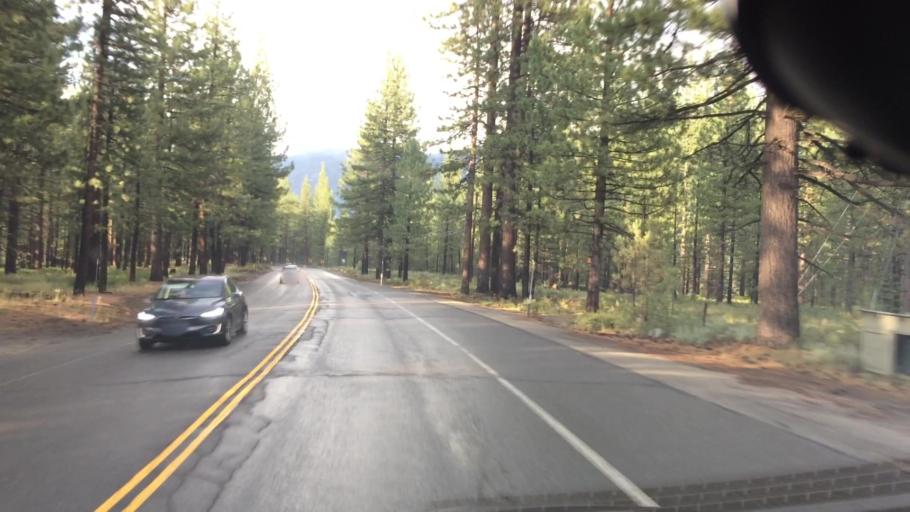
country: US
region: California
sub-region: El Dorado County
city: South Lake Tahoe
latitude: 38.8895
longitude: -119.9760
